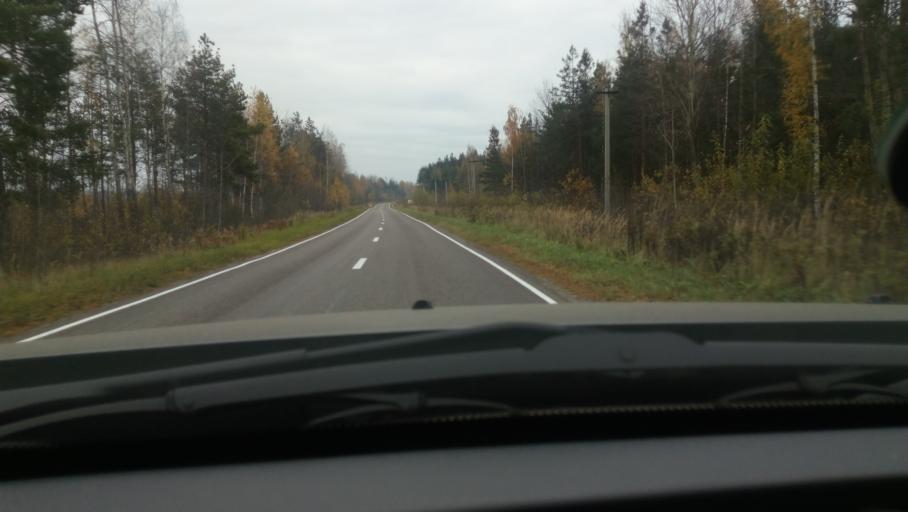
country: RU
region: Moskovskaya
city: Avsyunino
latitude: 55.5879
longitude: 39.2628
